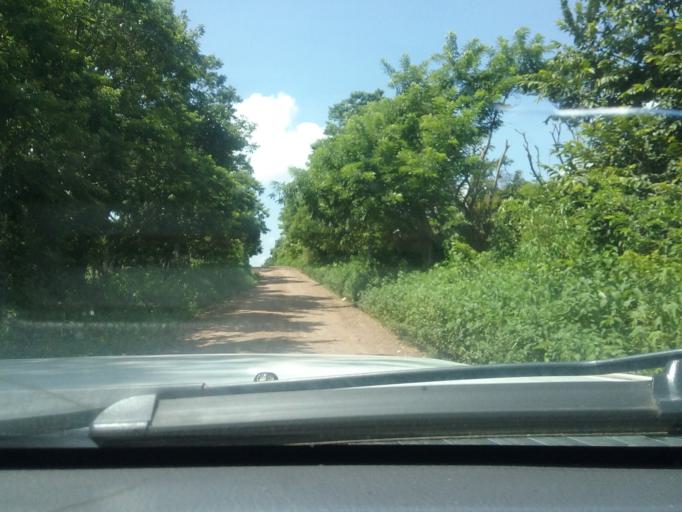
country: NI
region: Matagalpa
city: Terrabona
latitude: 12.6876
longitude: -85.9554
